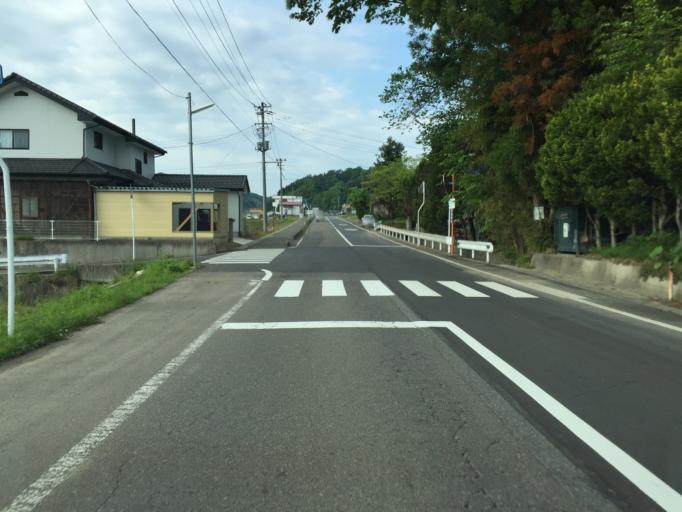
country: JP
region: Fukushima
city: Hobaramachi
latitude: 37.7270
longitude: 140.5986
